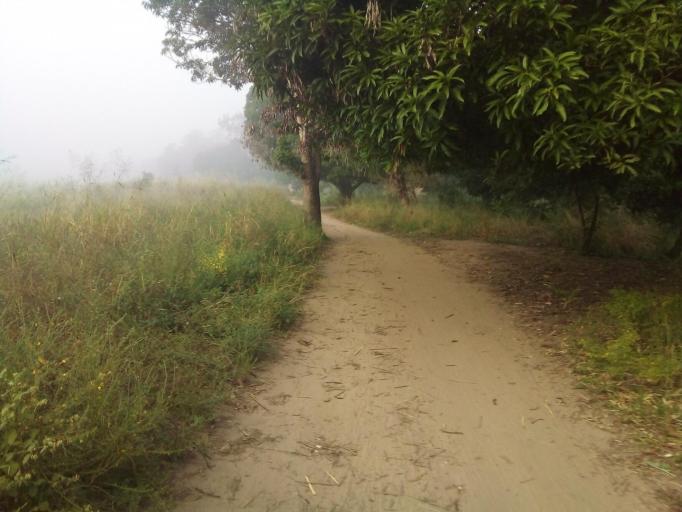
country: MZ
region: Zambezia
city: Quelimane
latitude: -17.5893
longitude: 36.6870
